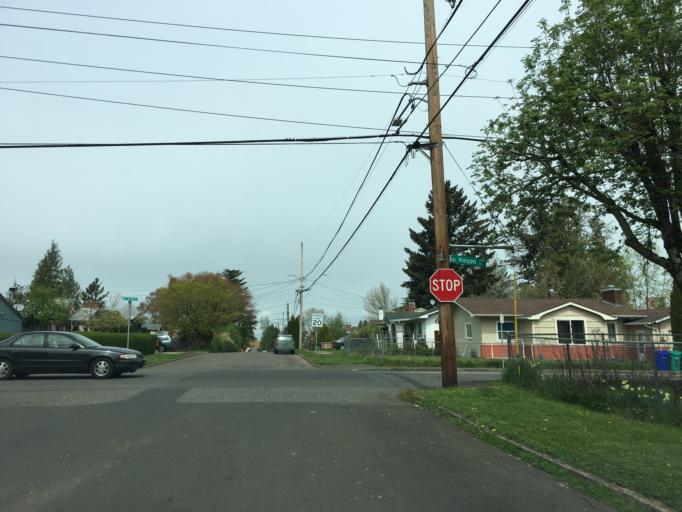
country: US
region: Oregon
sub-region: Multnomah County
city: Lents
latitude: 45.5552
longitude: -122.5746
